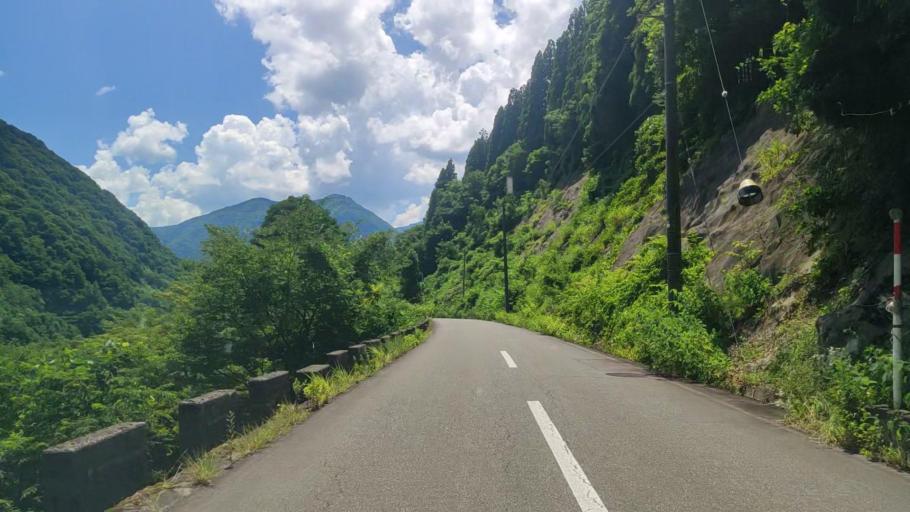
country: JP
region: Fukui
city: Ono
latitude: 35.8933
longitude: 136.5068
